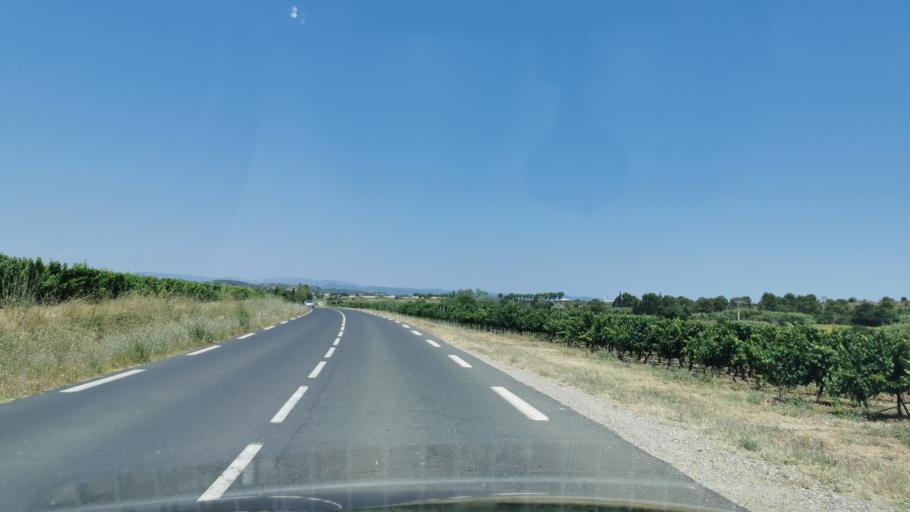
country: FR
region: Languedoc-Roussillon
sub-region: Departement de l'Herault
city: Cazouls-les-Beziers
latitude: 43.3732
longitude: 3.1129
